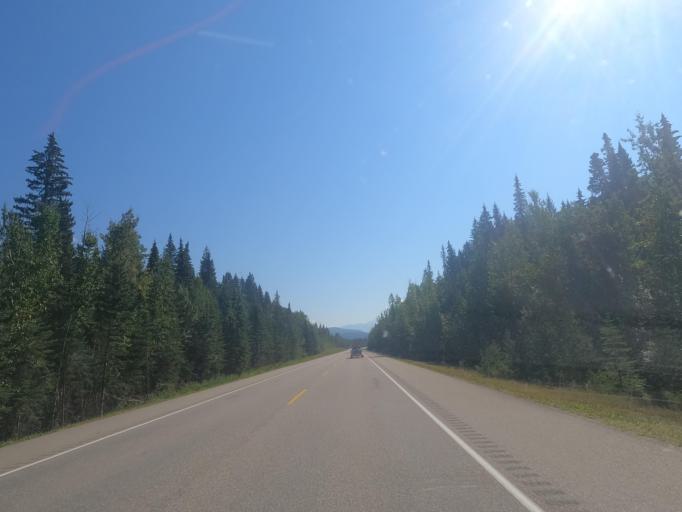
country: CA
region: Alberta
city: Jasper Park Lodge
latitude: 52.8766
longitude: -118.3252
